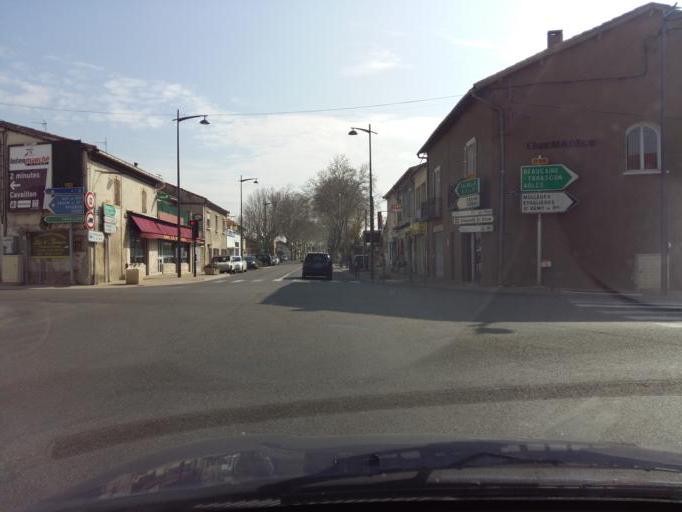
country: FR
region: Provence-Alpes-Cote d'Azur
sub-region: Departement des Bouches-du-Rhone
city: Molleges
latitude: 43.8076
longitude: 4.9952
